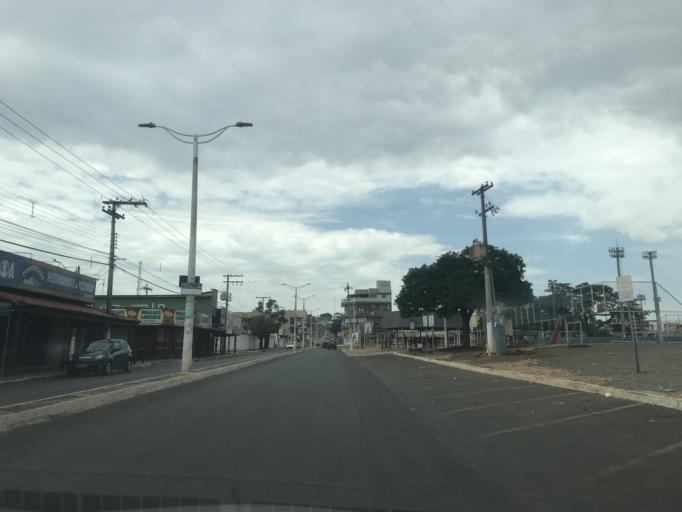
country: BR
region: Goias
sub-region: Luziania
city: Luziania
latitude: -16.2530
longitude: -47.9571
